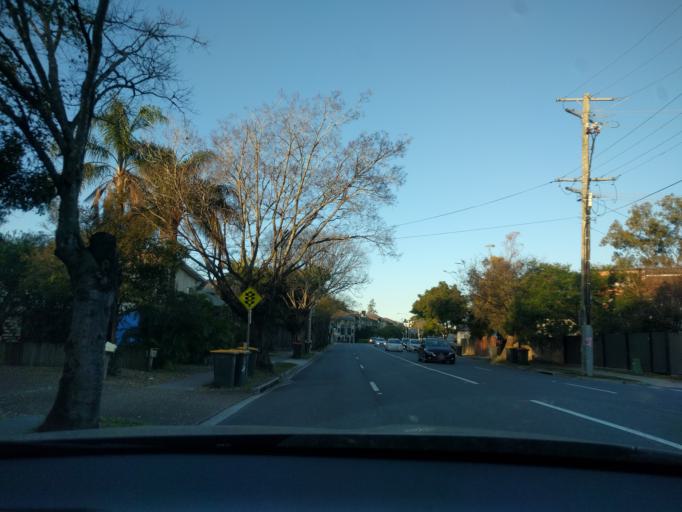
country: AU
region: Queensland
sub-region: Brisbane
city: Toowong
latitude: -27.4940
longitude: 153.0049
